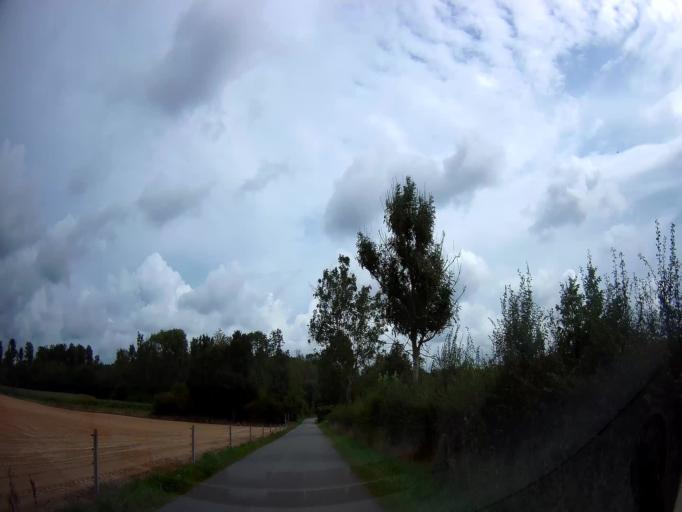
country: BE
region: Wallonia
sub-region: Province de Liege
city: Marchin
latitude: 50.4305
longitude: 5.2299
